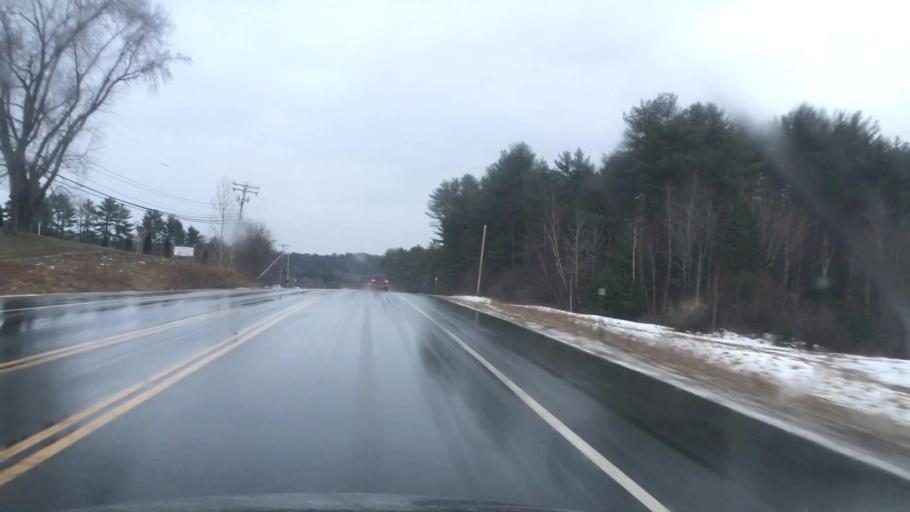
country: US
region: New Hampshire
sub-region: Sullivan County
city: Newport
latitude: 43.3651
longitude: -72.2353
